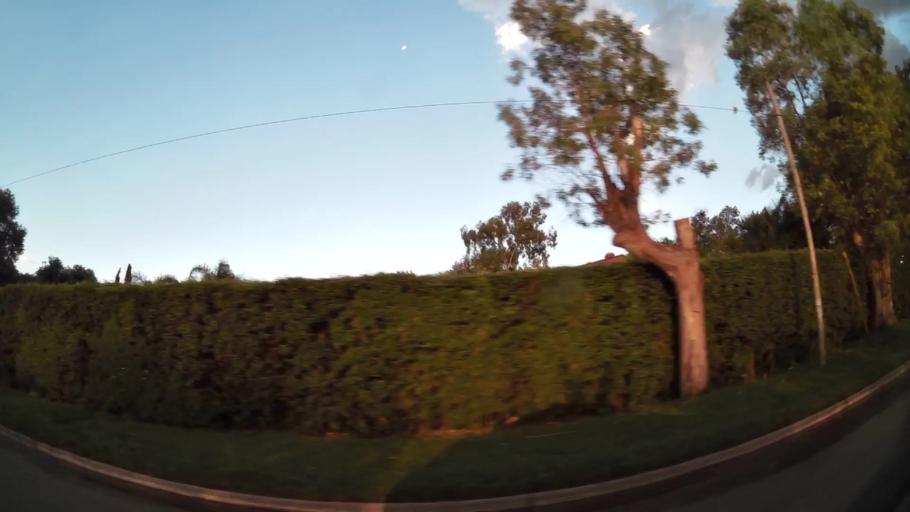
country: AR
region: Buenos Aires
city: Santa Catalina - Dique Lujan
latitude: -34.4802
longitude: -58.7537
